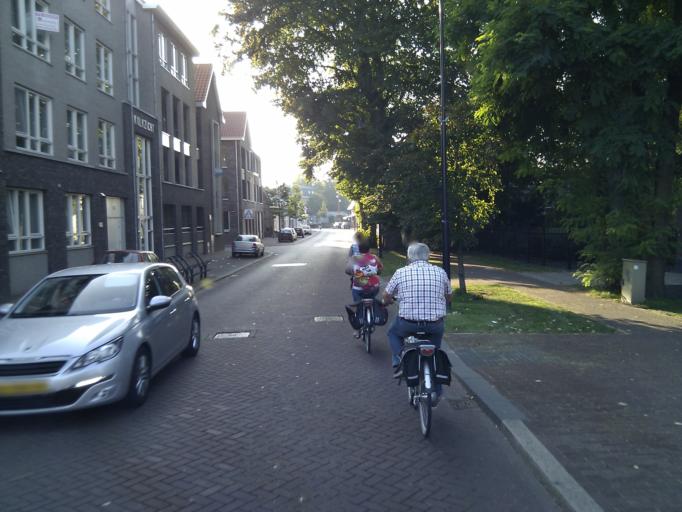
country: NL
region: North Brabant
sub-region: Gemeente Sint-Oedenrode
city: Sint-Oedenrode
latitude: 51.5655
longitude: 5.4648
